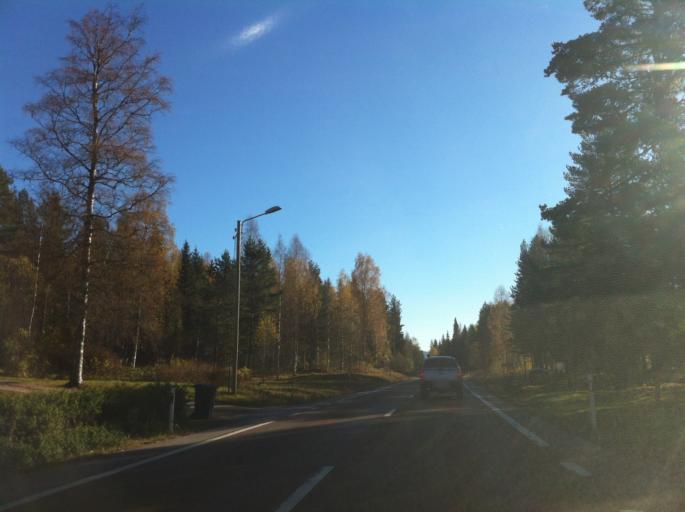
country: SE
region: Dalarna
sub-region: Alvdalens Kommun
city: AElvdalen
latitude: 61.1765
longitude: 14.1000
